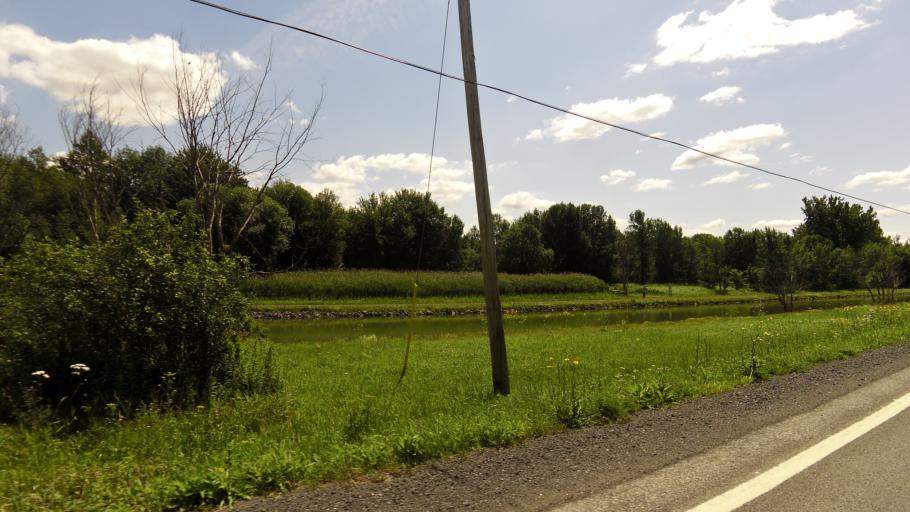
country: CA
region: Quebec
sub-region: Monteregie
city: Richelieu
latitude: 45.3898
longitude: -73.2595
